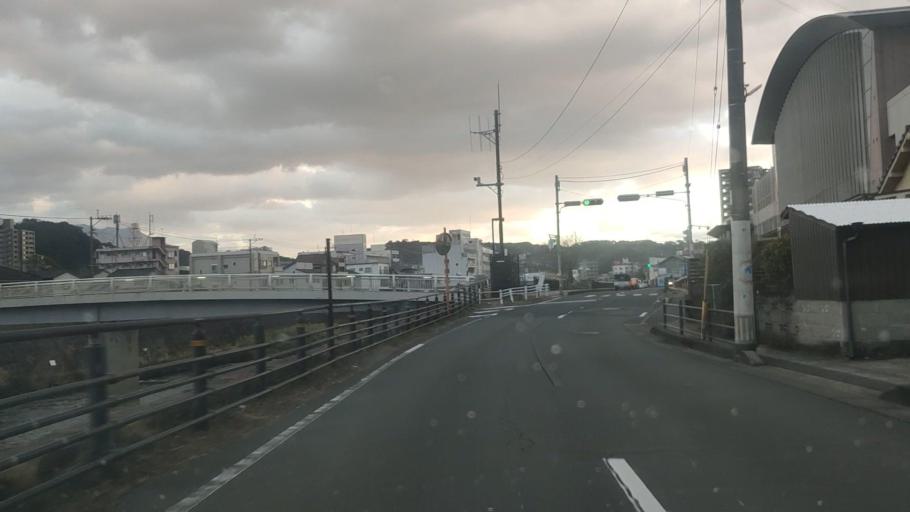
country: JP
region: Kagoshima
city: Kagoshima-shi
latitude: 31.6106
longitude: 130.5321
